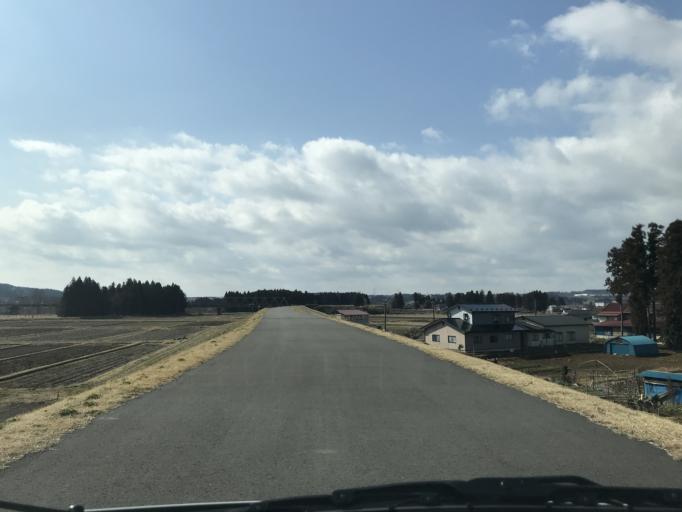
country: JP
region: Iwate
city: Mizusawa
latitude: 39.0458
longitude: 141.1467
